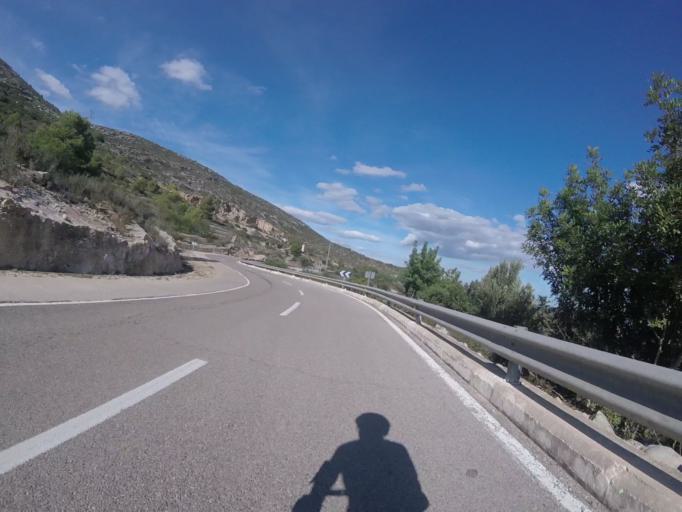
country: ES
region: Valencia
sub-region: Provincia de Castello
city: Alcala de Xivert
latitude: 40.2965
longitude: 0.1866
